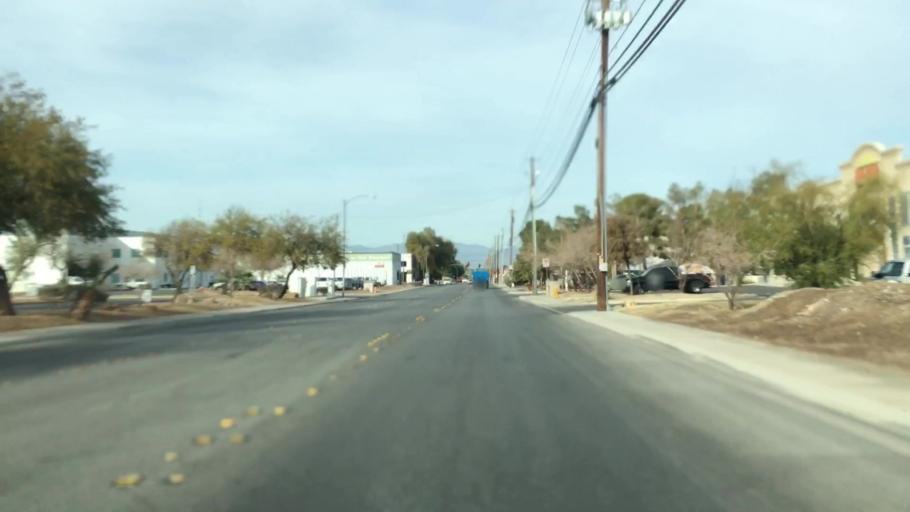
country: US
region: Nevada
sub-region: Clark County
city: Whitney
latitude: 36.0758
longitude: -115.0870
